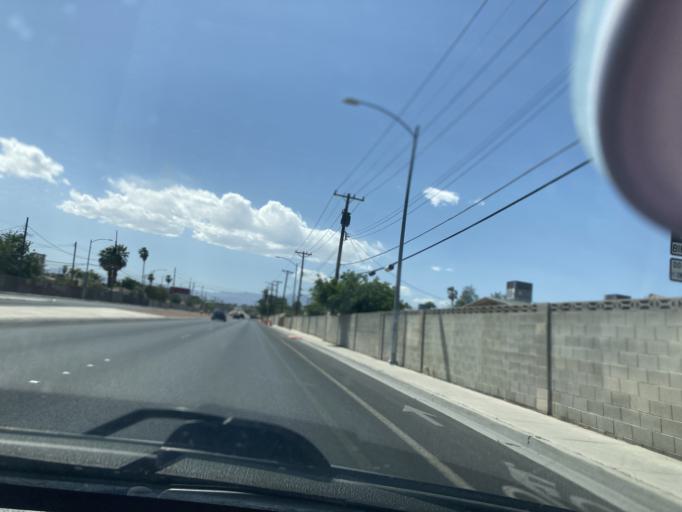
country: US
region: Nevada
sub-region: Clark County
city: North Las Vegas
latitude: 36.1812
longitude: -115.1120
